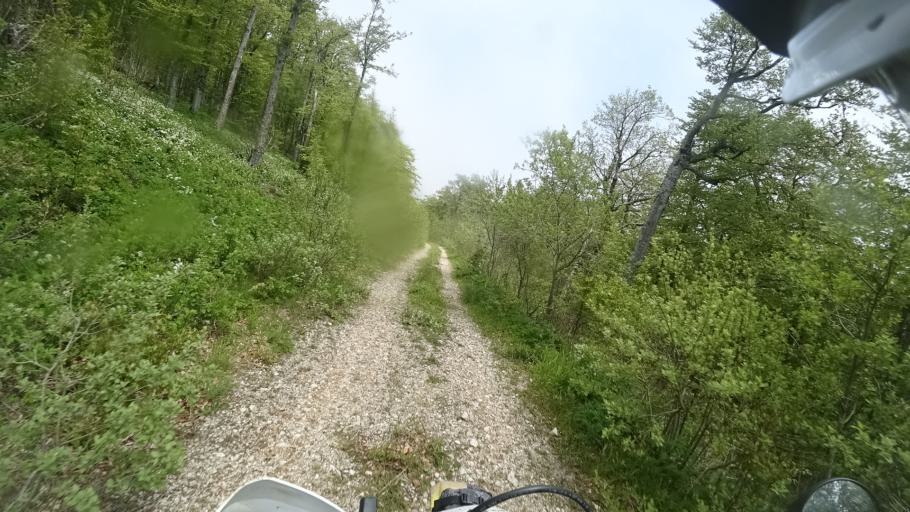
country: BA
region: Federation of Bosnia and Herzegovina
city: Orasac
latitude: 44.5699
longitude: 15.8758
